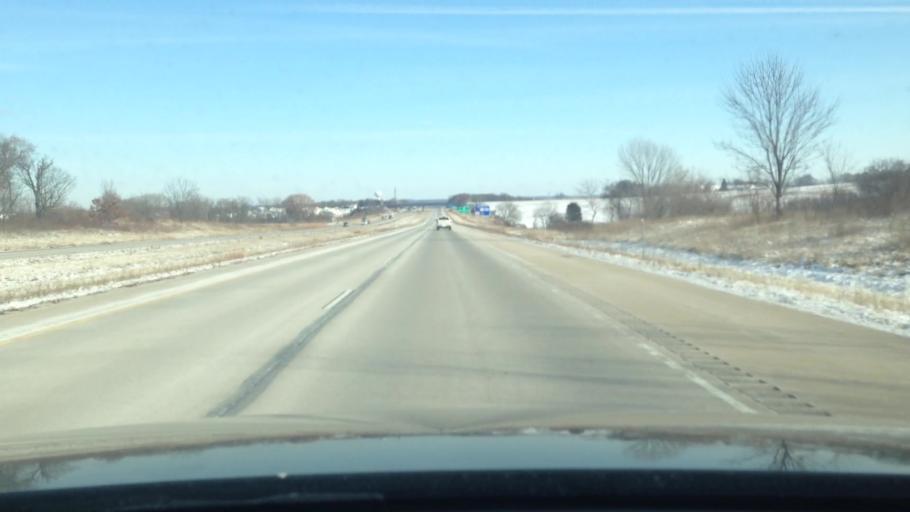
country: US
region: Wisconsin
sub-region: Walworth County
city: Potter Lake
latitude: 42.8338
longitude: -88.3447
